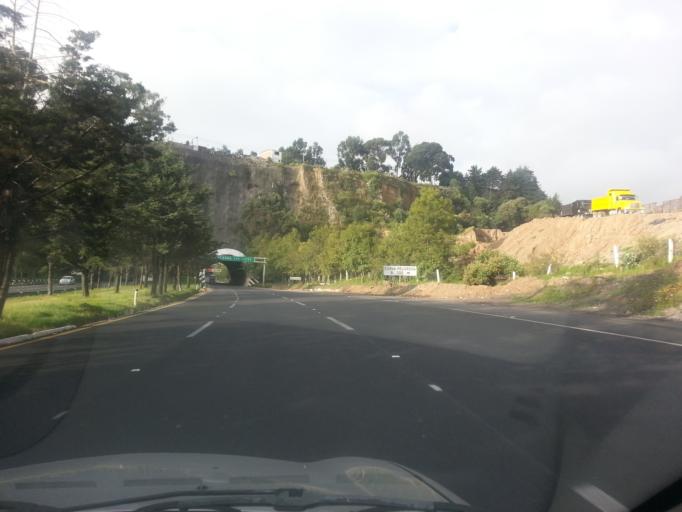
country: MX
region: Mexico City
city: Cuajimalpa
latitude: 19.3545
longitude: -99.2792
